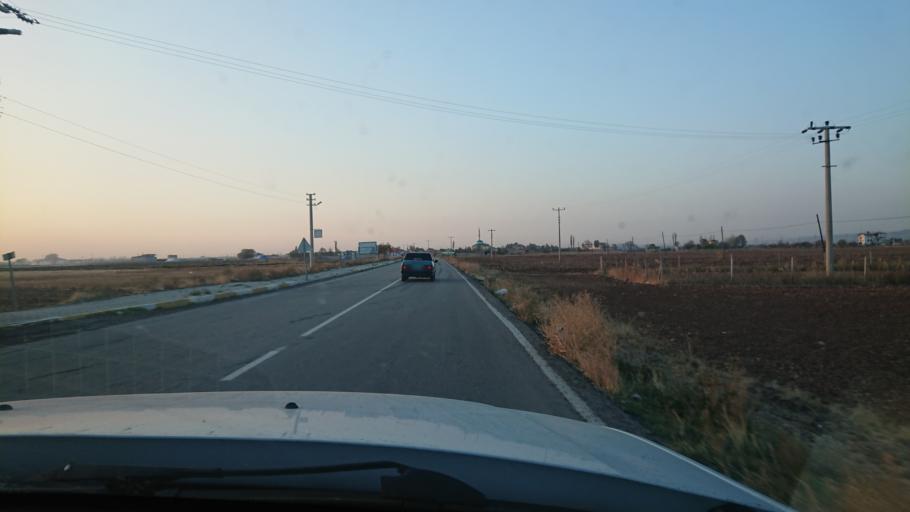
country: TR
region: Aksaray
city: Aksaray
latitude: 38.3134
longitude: 34.0595
